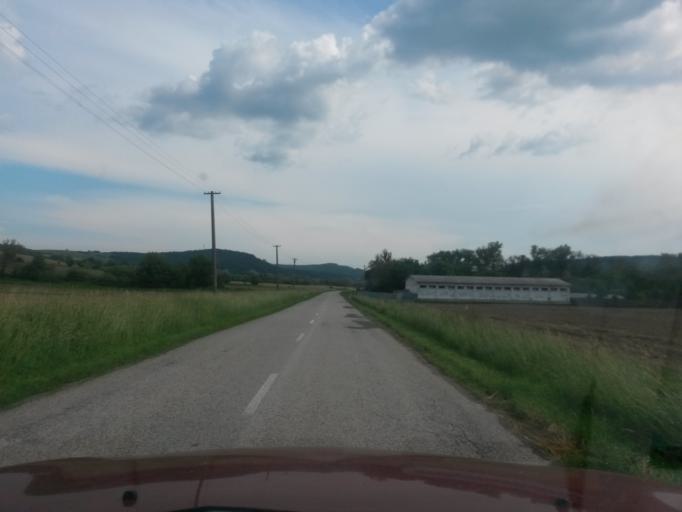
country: SK
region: Presovsky
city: Snina
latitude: 49.0865
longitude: 22.0615
